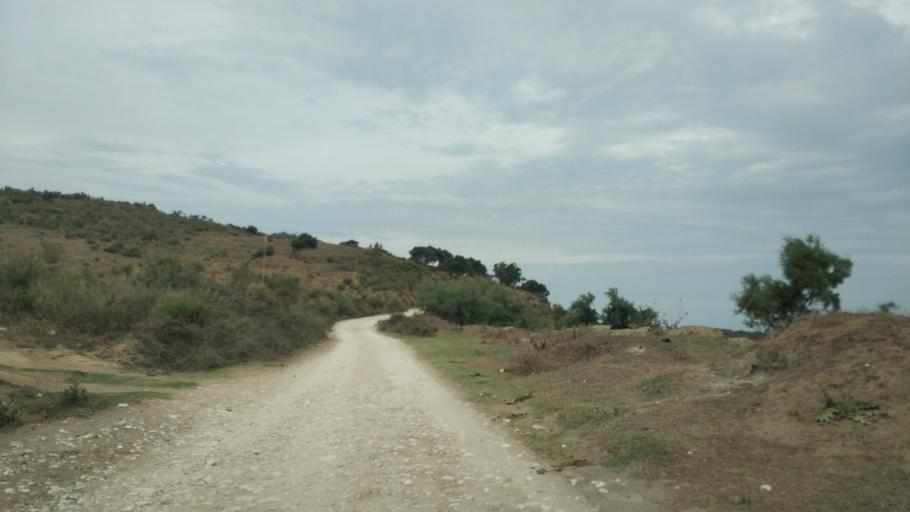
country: AL
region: Vlore
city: Vlore
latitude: 40.5153
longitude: 19.3950
